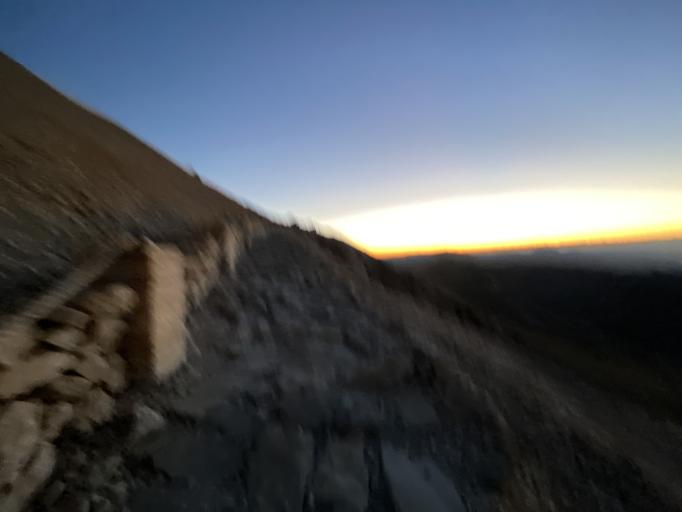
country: TR
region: Adiyaman
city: Narince
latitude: 37.9803
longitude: 38.7416
